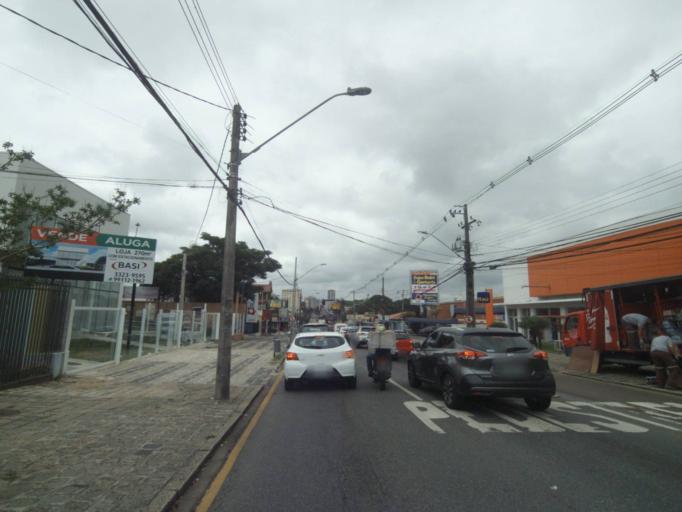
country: BR
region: Parana
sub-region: Curitiba
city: Curitiba
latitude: -25.4273
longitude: -49.2469
